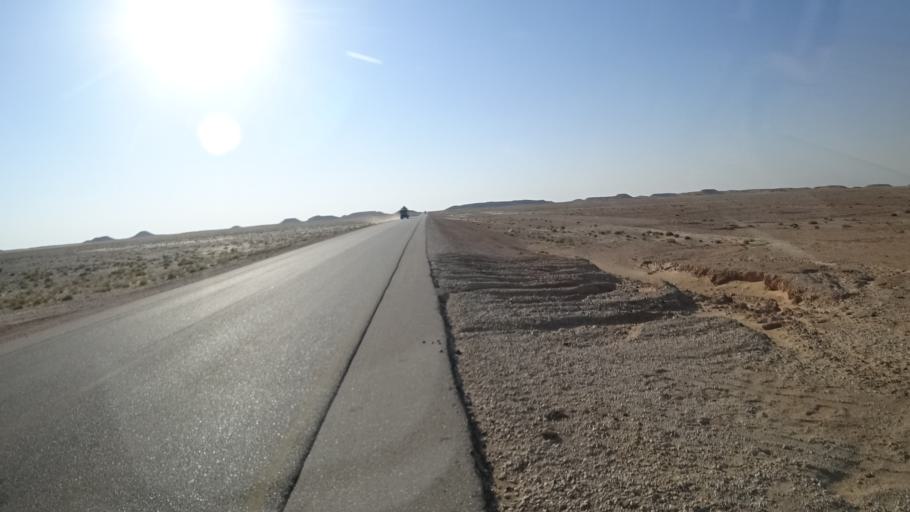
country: OM
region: Zufar
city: Salalah
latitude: 17.6416
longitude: 53.8234
